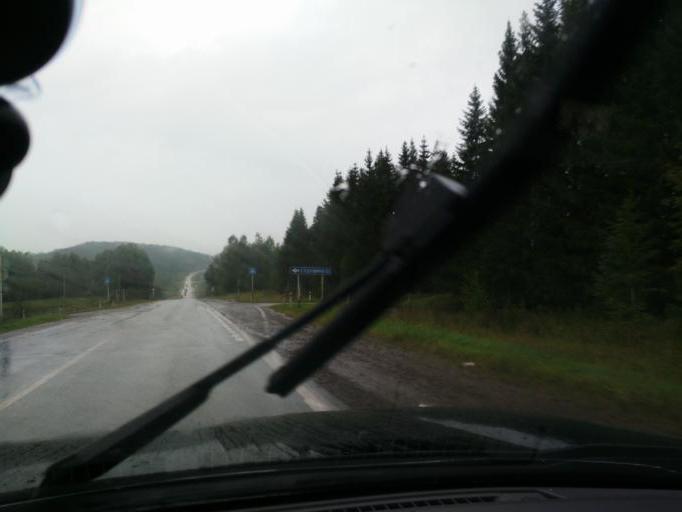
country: RU
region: Perm
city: Osa
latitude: 57.2936
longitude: 55.6109
